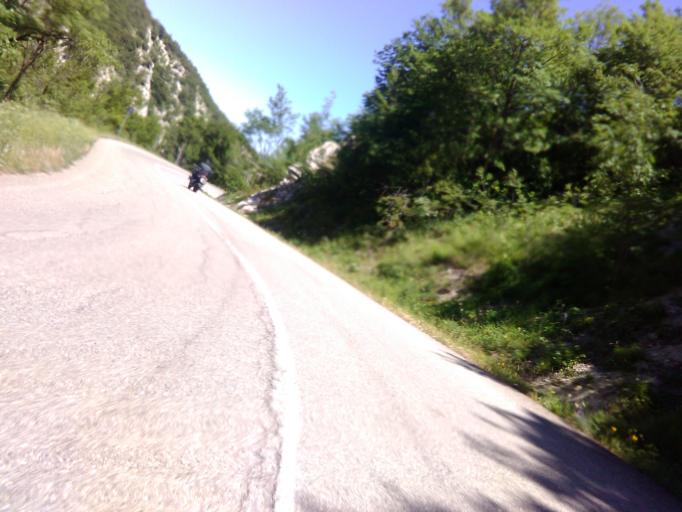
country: IT
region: Emilia-Romagna
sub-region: Provincia di Parma
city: Calestano
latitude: 44.5883
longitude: 10.1082
